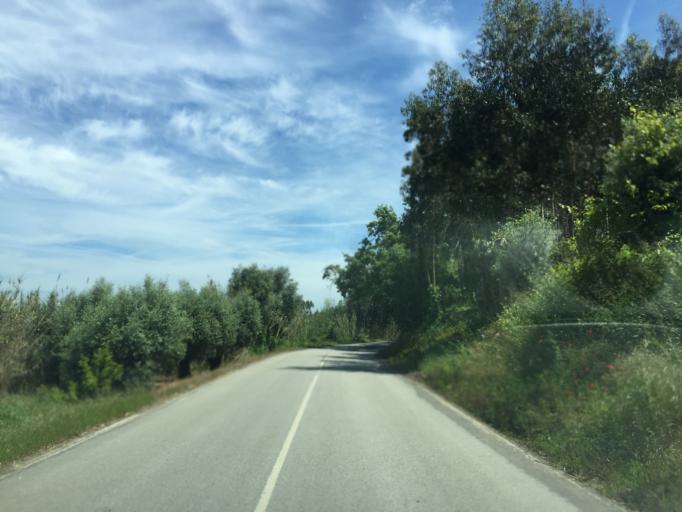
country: PT
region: Leiria
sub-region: Pombal
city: Lourical
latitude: 40.0664
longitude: -8.7560
